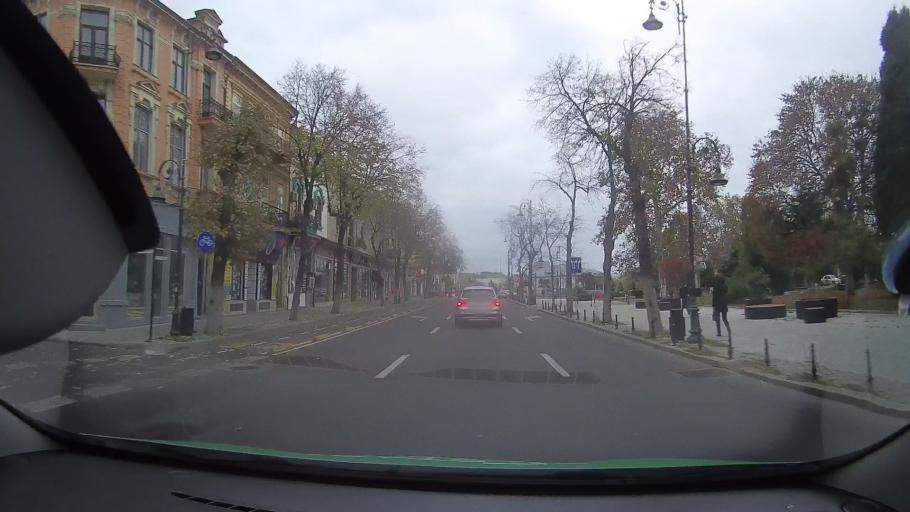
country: RO
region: Constanta
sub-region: Municipiul Constanta
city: Constanta
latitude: 44.1773
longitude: 28.6529
